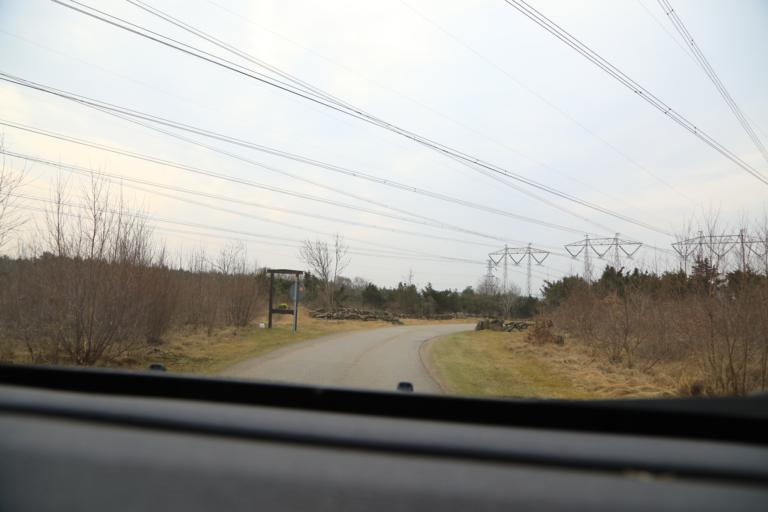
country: SE
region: Halland
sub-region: Kungsbacka Kommun
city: Frillesas
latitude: 57.2656
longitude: 12.1218
